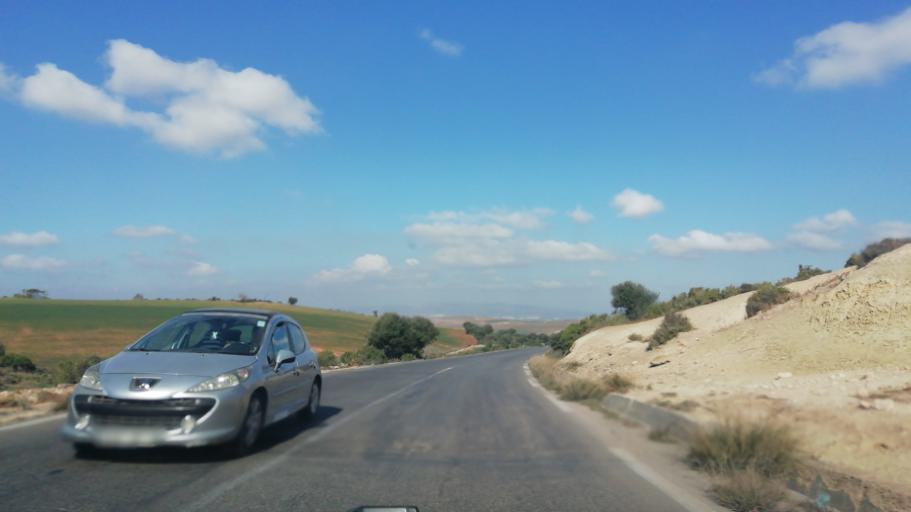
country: DZ
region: Oran
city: Ain el Bya
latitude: 35.7234
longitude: -0.2442
